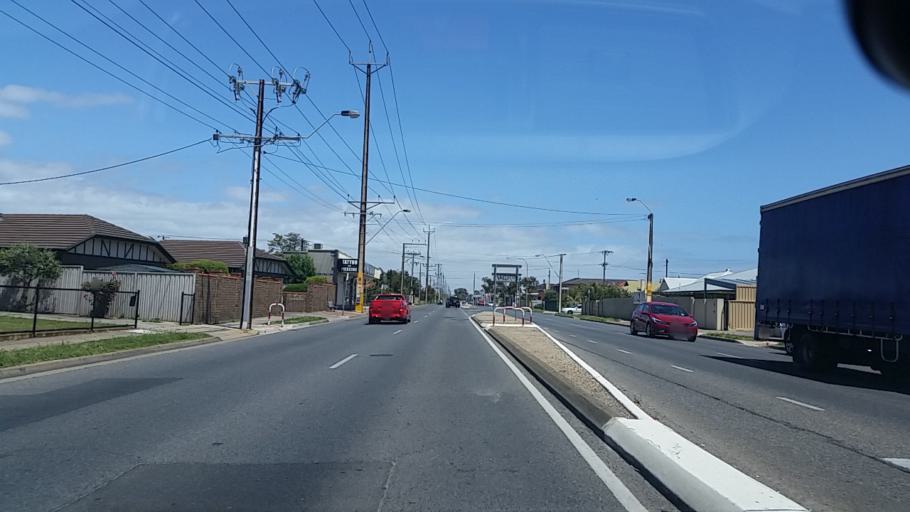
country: AU
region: South Australia
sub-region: Charles Sturt
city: Woodville West
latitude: -34.8876
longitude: 138.5313
